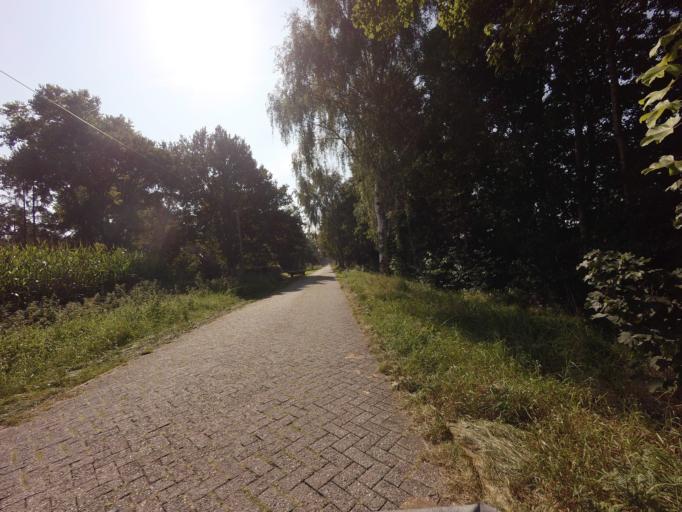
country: DE
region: Lower Saxony
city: Emlichheim
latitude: 52.5925
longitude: 6.8334
